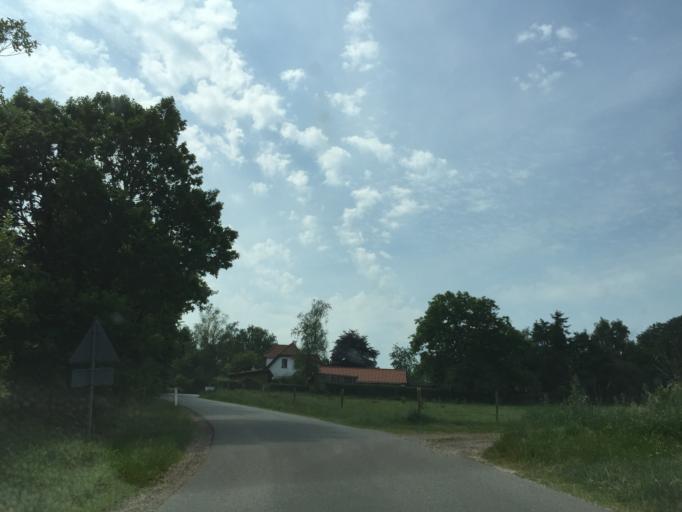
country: DK
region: Central Jutland
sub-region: Silkeborg Kommune
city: Virklund
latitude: 56.0422
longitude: 9.4526
